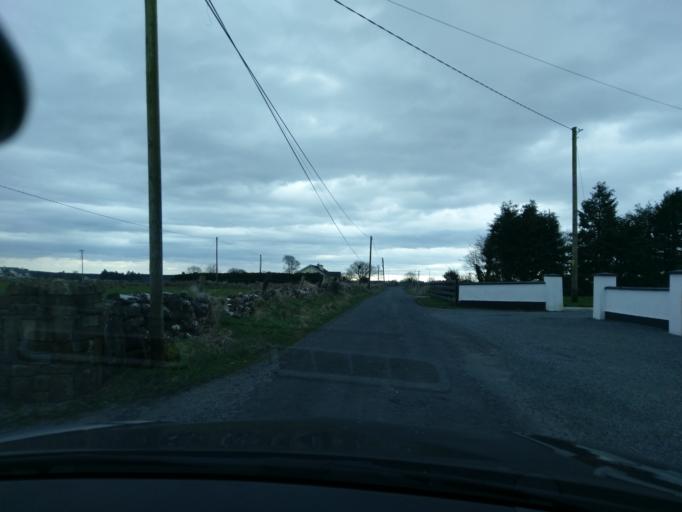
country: IE
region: Connaught
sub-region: County Galway
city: Athenry
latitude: 53.3890
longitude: -8.6460
